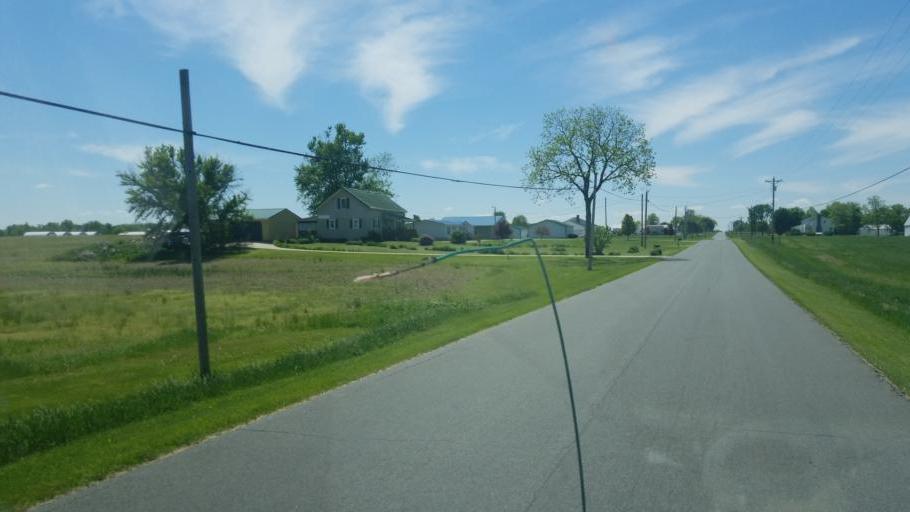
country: US
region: Ohio
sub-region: Huron County
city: Willard
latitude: 41.0834
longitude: -82.7604
